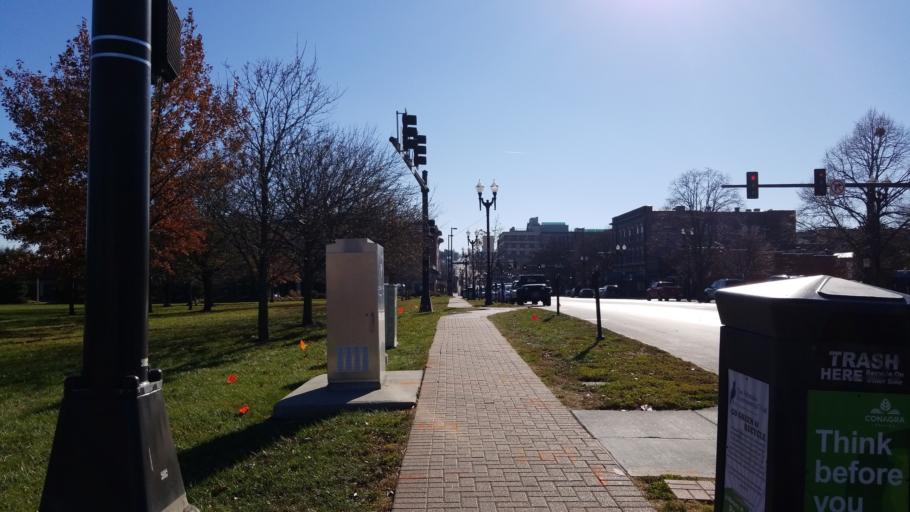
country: US
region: Nebraska
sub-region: Douglas County
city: Omaha
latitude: 41.2567
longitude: -95.9291
